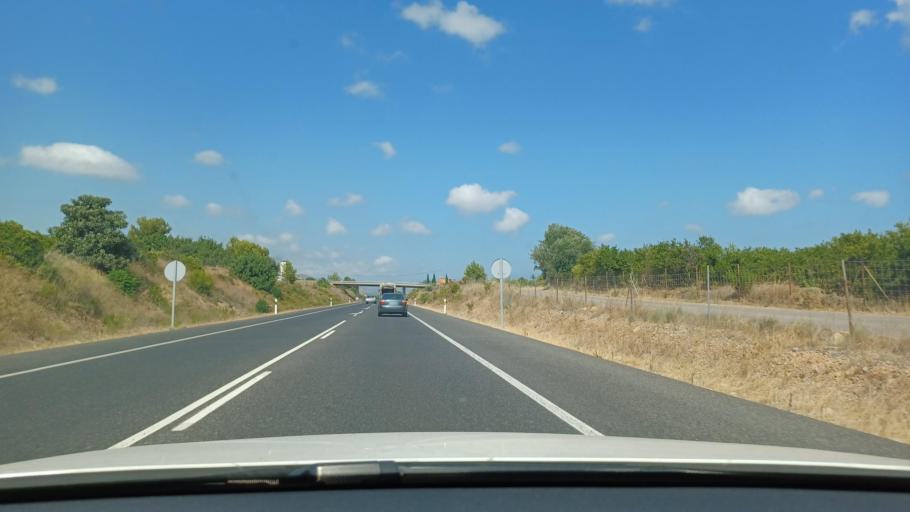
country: ES
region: Valencia
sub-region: Provincia de Castello
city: Castello de la Plana
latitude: 40.0062
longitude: -0.0593
